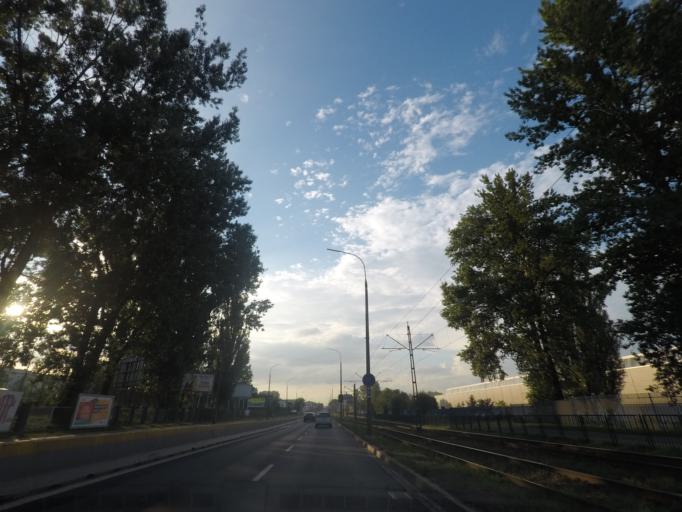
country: PL
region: Lesser Poland Voivodeship
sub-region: Krakow
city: Krakow
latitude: 50.0292
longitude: 19.9746
